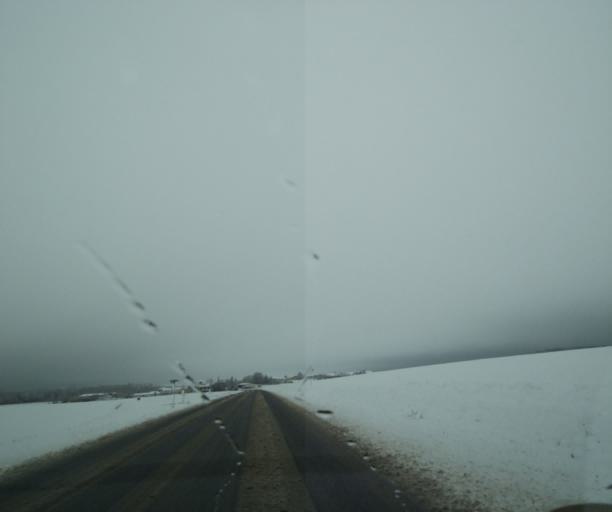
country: FR
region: Champagne-Ardenne
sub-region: Departement de la Haute-Marne
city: Wassy
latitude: 48.5196
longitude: 4.9341
